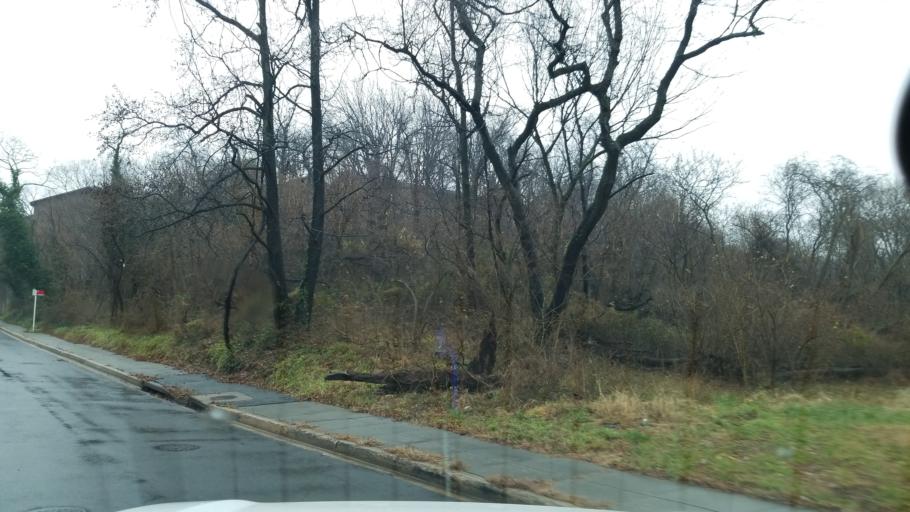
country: US
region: Maryland
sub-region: Prince George's County
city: Glassmanor
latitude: 38.8557
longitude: -76.9932
